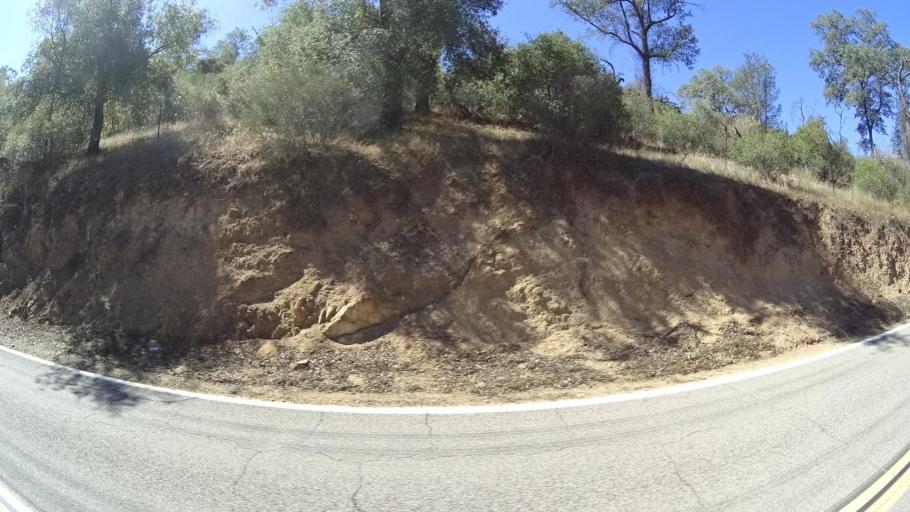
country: US
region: California
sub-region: San Diego County
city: Alpine
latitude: 32.7107
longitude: -116.7430
